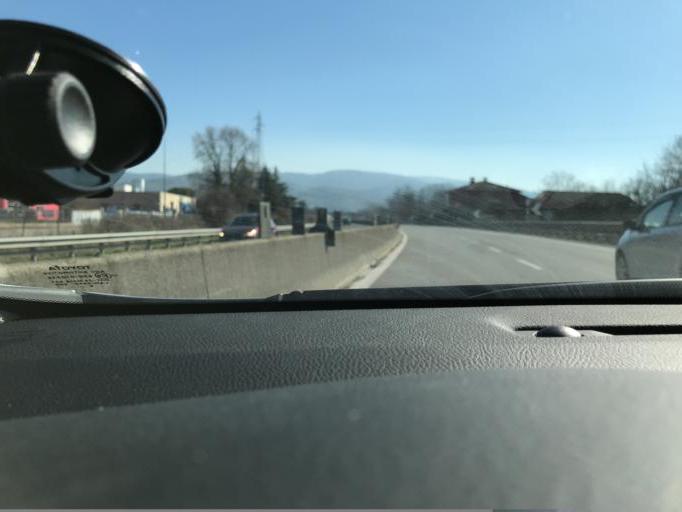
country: IT
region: Umbria
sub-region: Provincia di Perugia
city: San Martino in Campo
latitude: 43.0223
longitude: 12.4146
